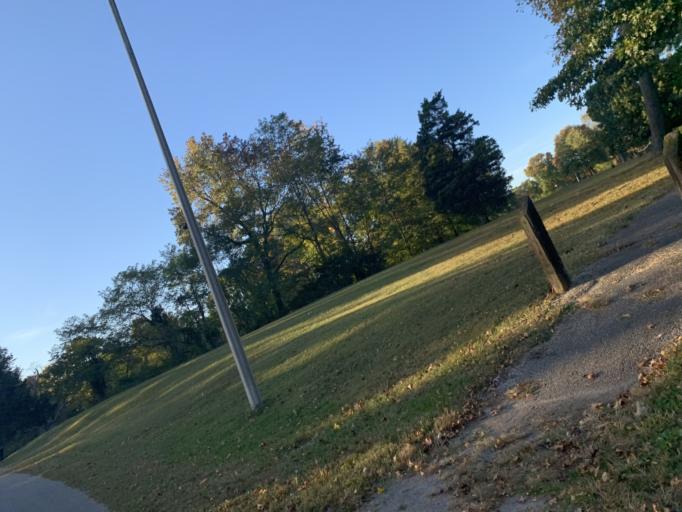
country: US
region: Kentucky
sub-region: Jefferson County
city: Shively
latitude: 38.2392
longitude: -85.8310
